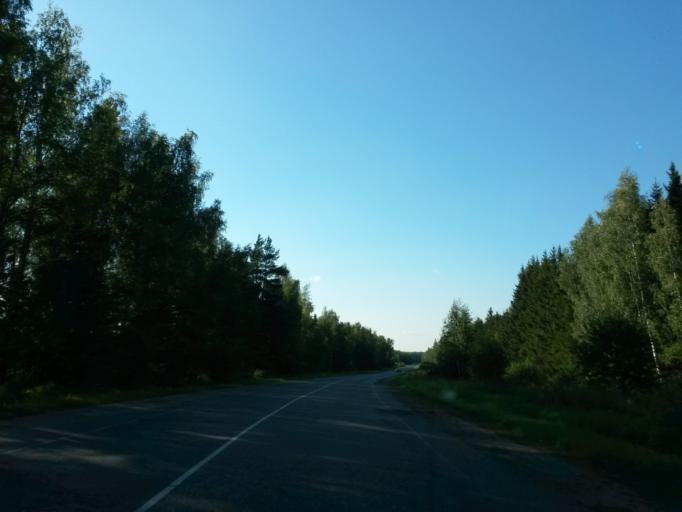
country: RU
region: Ivanovo
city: Pistsovo
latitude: 57.0914
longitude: 40.6635
